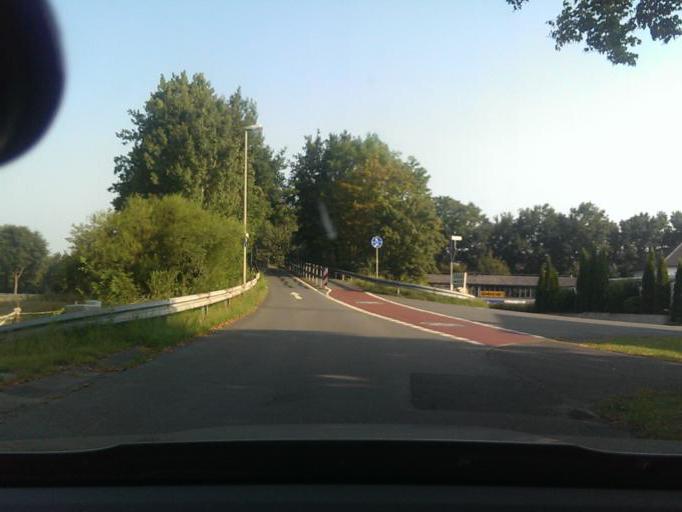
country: DE
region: North Rhine-Westphalia
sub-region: Regierungsbezirk Detmold
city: Delbruck
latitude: 51.7617
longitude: 8.5675
